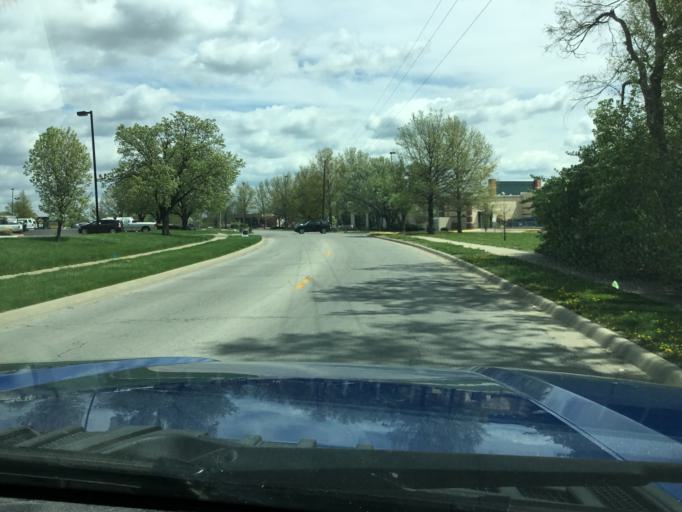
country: US
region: Kansas
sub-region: Douglas County
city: Lawrence
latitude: 38.9347
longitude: -95.2638
